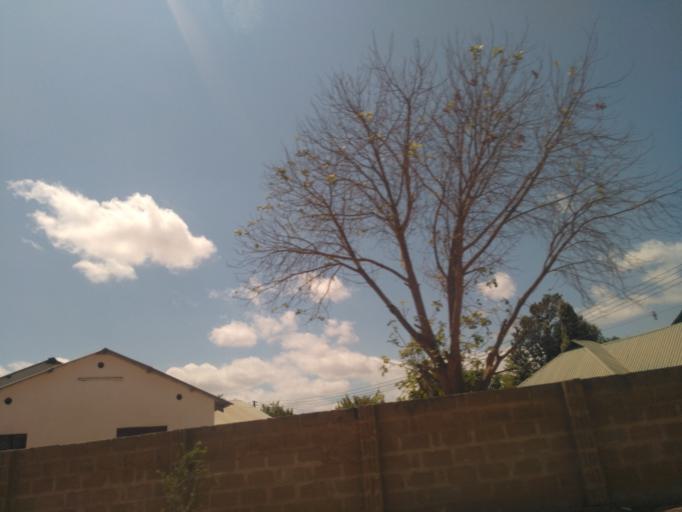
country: TZ
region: Dodoma
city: Kisasa
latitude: -6.1690
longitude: 35.7709
